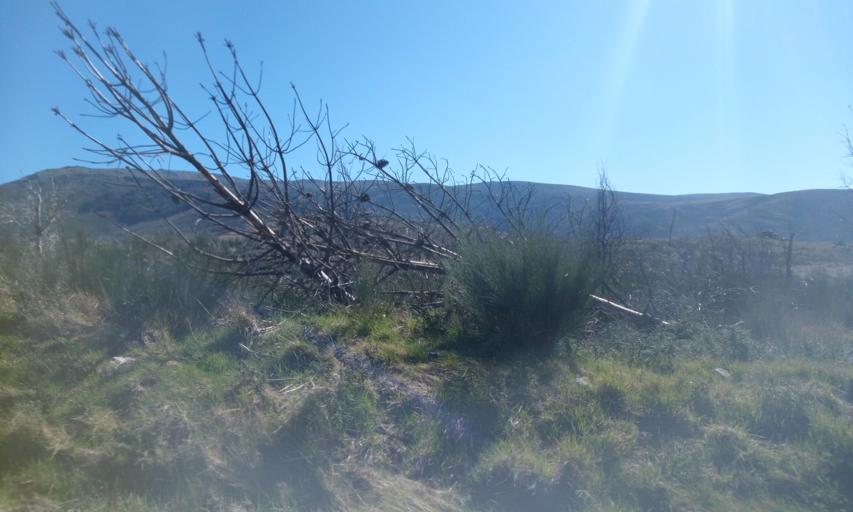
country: PT
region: Guarda
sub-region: Manteigas
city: Manteigas
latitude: 40.4915
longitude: -7.5687
